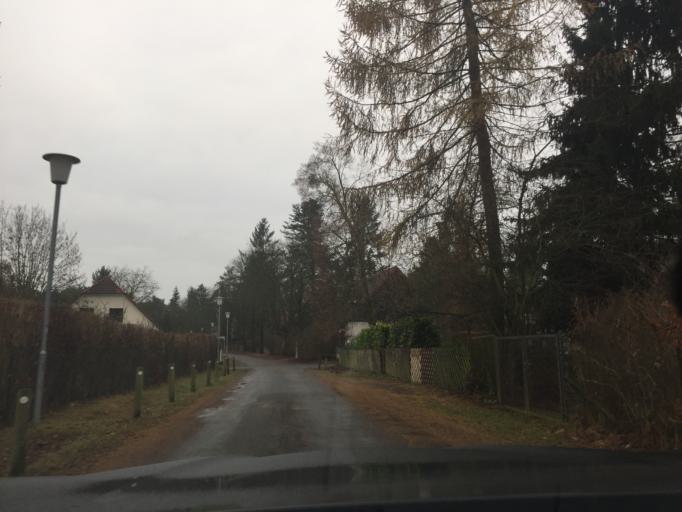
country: DE
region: Berlin
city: Kladow
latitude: 52.4588
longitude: 13.1028
